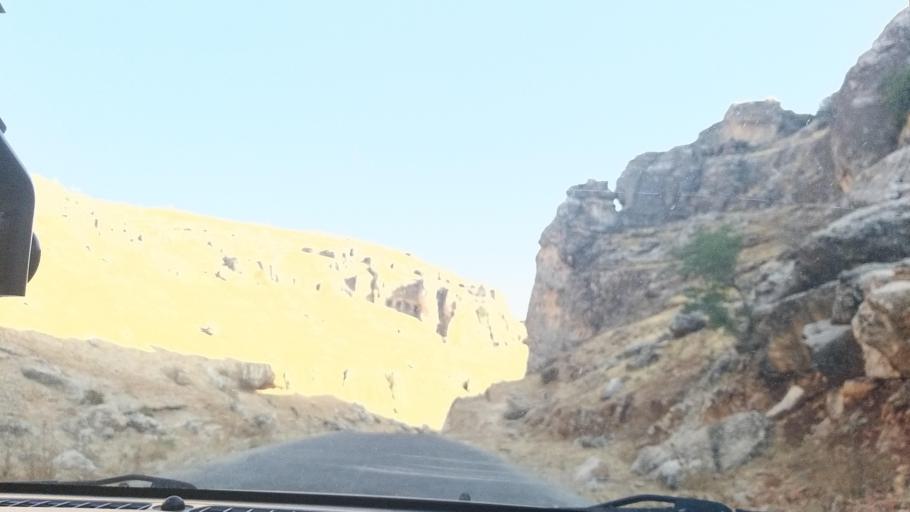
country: TR
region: Diyarbakir
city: Silvan
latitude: 38.1670
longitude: 41.0016
